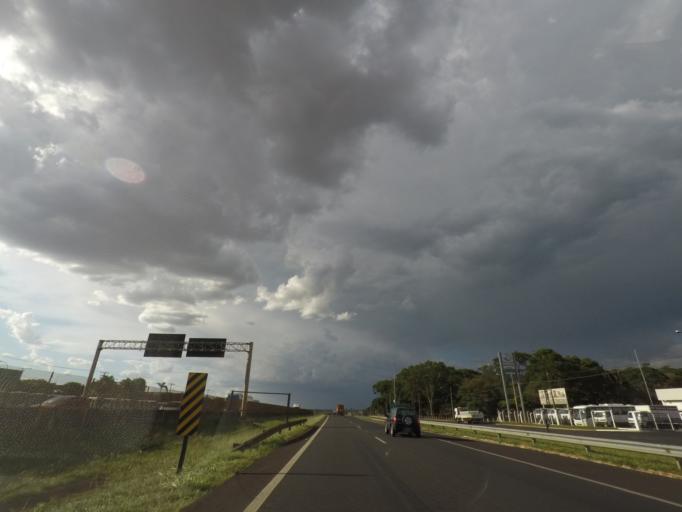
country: BR
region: Sao Paulo
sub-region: Ribeirao Preto
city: Ribeirao Preto
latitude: -21.1413
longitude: -47.7609
